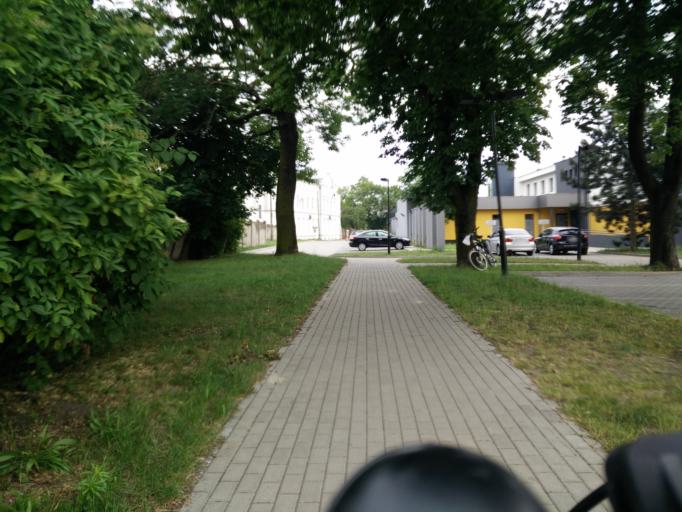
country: PL
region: Greater Poland Voivodeship
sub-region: Powiat sredzki
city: Sroda Wielkopolska
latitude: 52.2186
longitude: 17.2747
